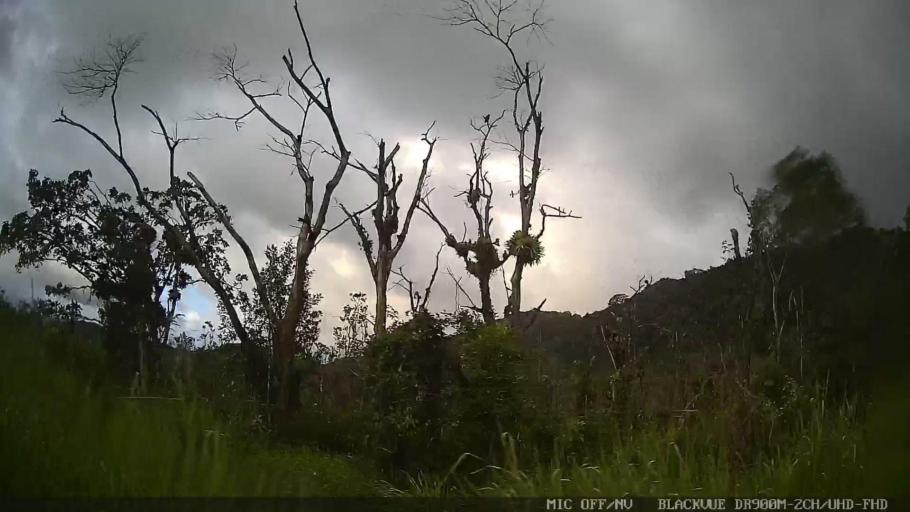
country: BR
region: Sao Paulo
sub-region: Itanhaem
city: Itanhaem
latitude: -24.1389
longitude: -46.7768
